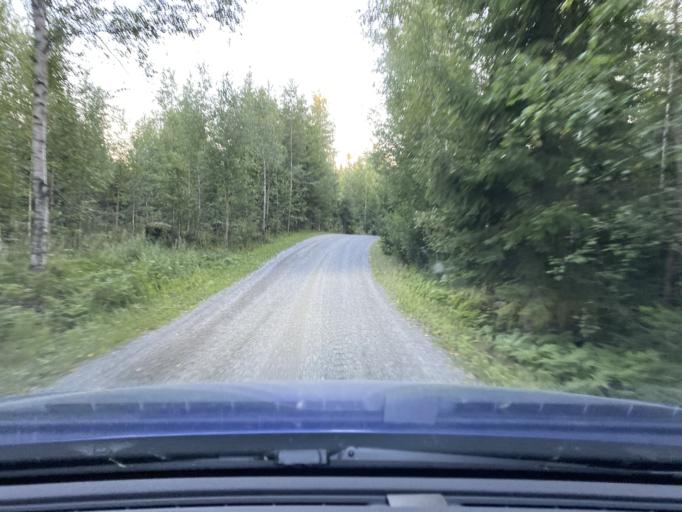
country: FI
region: Satakunta
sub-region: Rauma
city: Kiukainen
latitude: 61.1365
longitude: 22.0223
